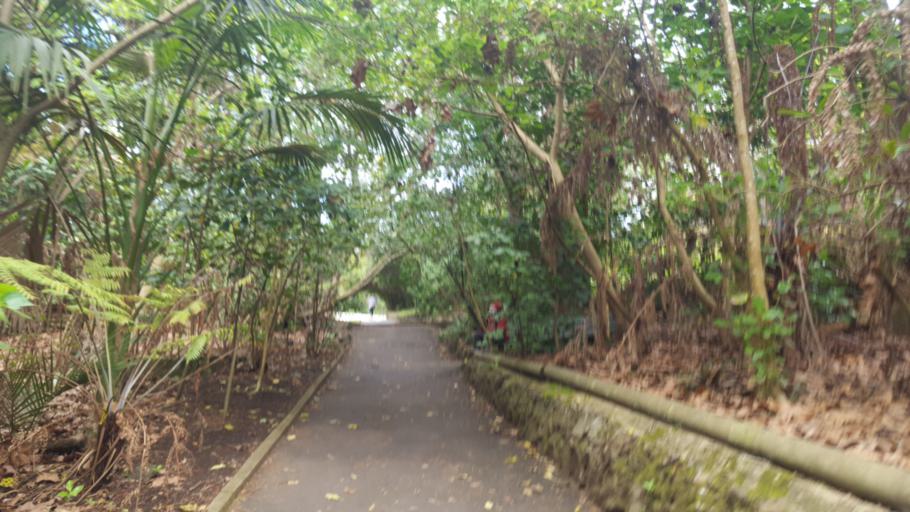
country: NZ
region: Auckland
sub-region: Auckland
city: Auckland
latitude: -36.8741
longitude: 174.7639
